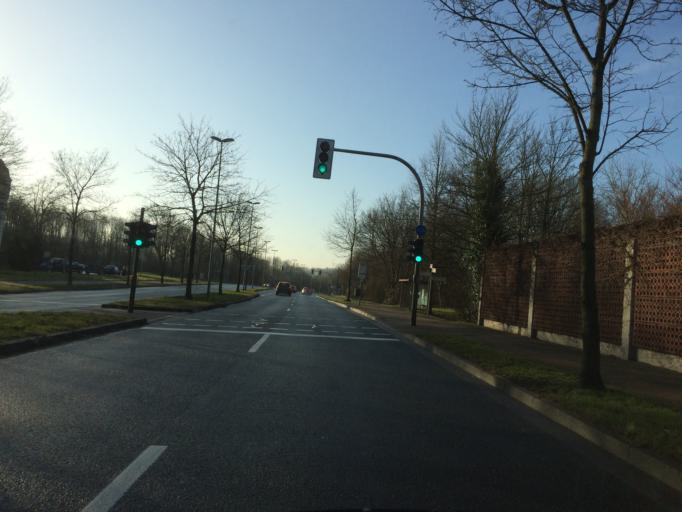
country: DE
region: North Rhine-Westphalia
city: Bochum-Hordel
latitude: 51.5176
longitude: 7.1901
